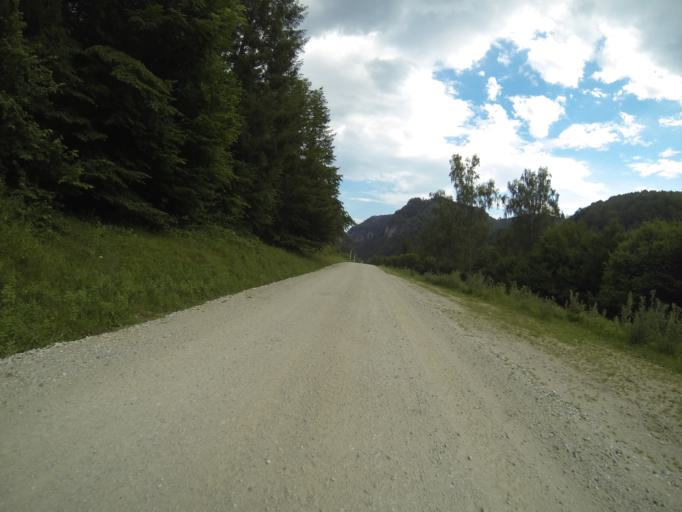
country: RO
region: Gorj
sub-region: Comuna Polovragi
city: Polovragi
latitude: 45.2180
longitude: 23.7734
